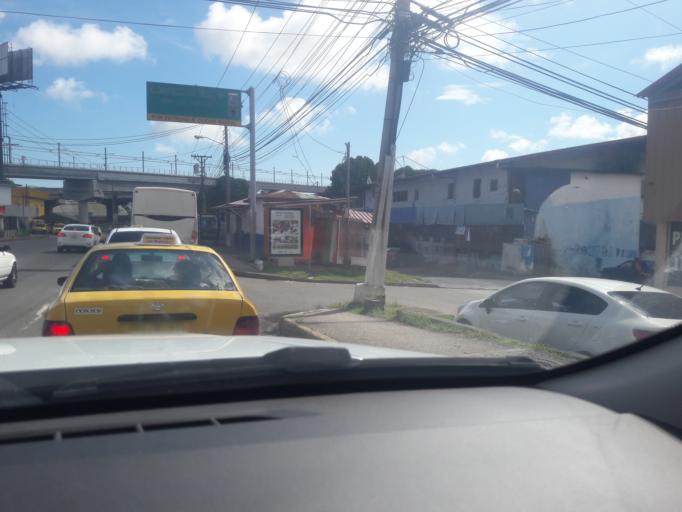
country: PA
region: Panama
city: San Miguelito
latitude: 9.0596
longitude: -79.4323
